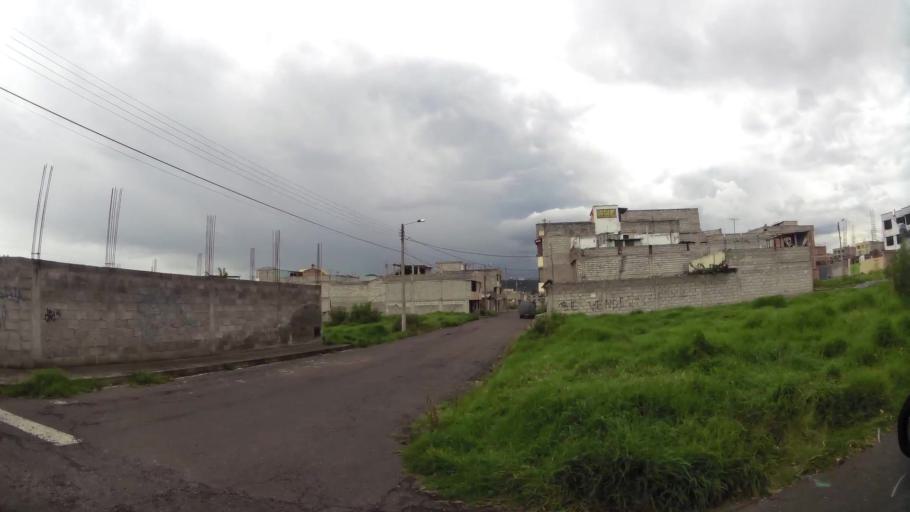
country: EC
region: Pichincha
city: Quito
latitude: -0.3123
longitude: -78.5560
